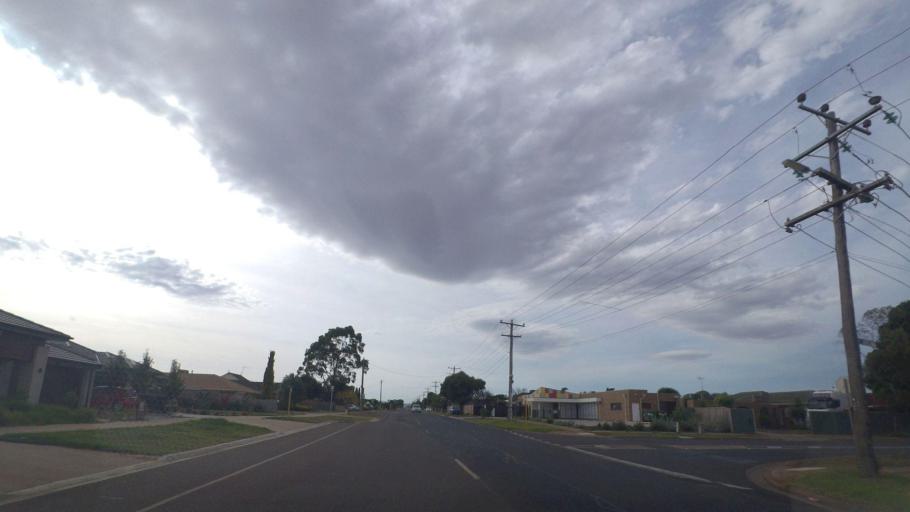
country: AU
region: Victoria
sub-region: Melton
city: Brookfield
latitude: -37.7130
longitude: 144.5628
